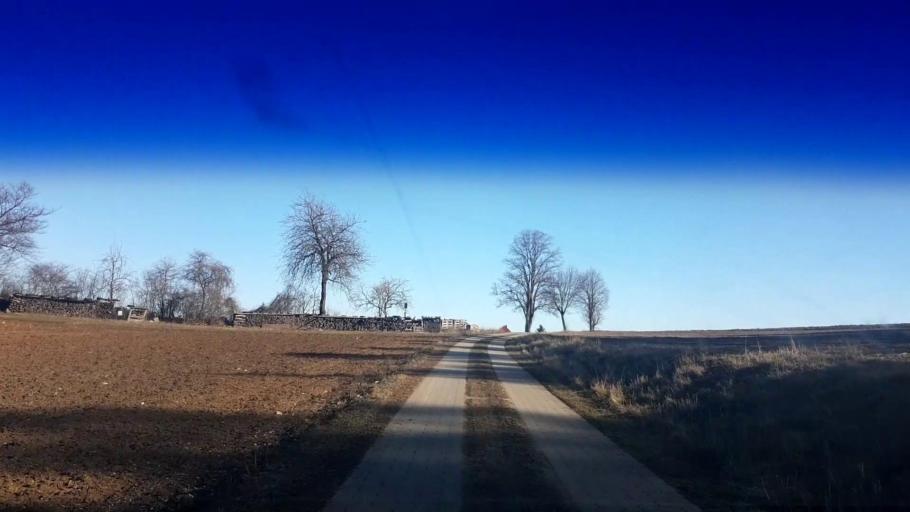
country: DE
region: Bavaria
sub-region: Upper Franconia
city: Poxdorf
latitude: 49.9654
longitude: 11.0957
